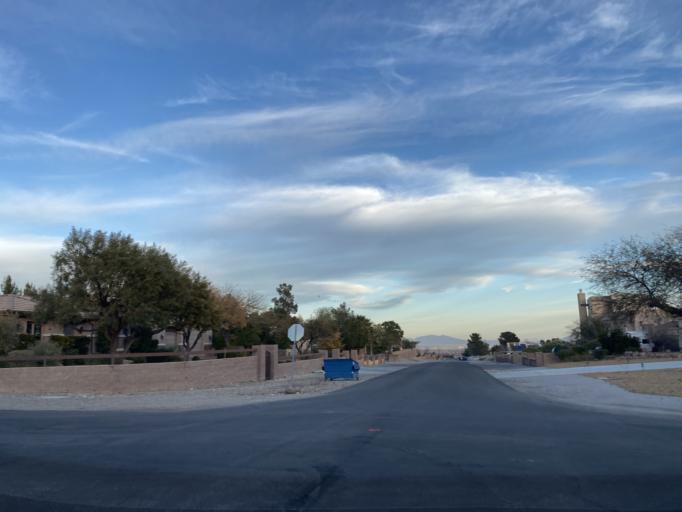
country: US
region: Nevada
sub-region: Clark County
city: Summerlin South
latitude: 36.2903
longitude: -115.3127
